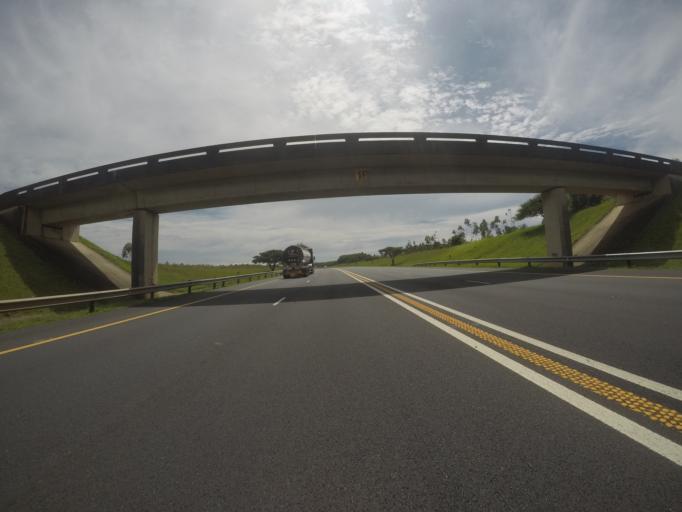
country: ZA
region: KwaZulu-Natal
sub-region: iLembe District Municipality
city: Mandeni
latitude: -29.1624
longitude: 31.5329
